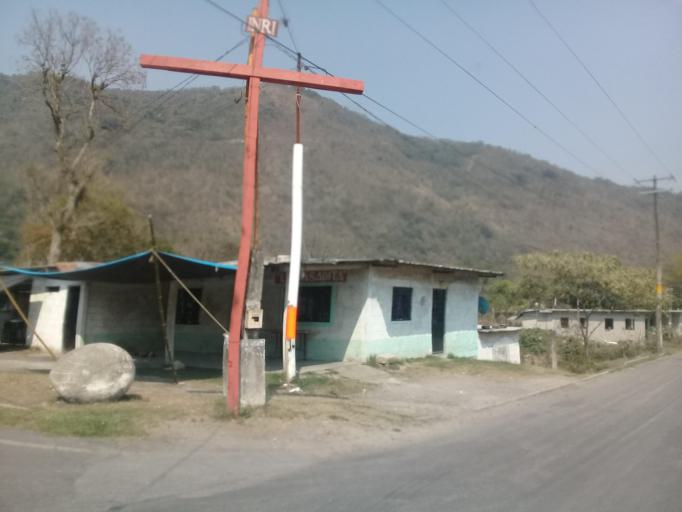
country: MX
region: Veracruz
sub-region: Ixtaczoquitlan
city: Campo Chico
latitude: 18.8340
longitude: -97.0239
